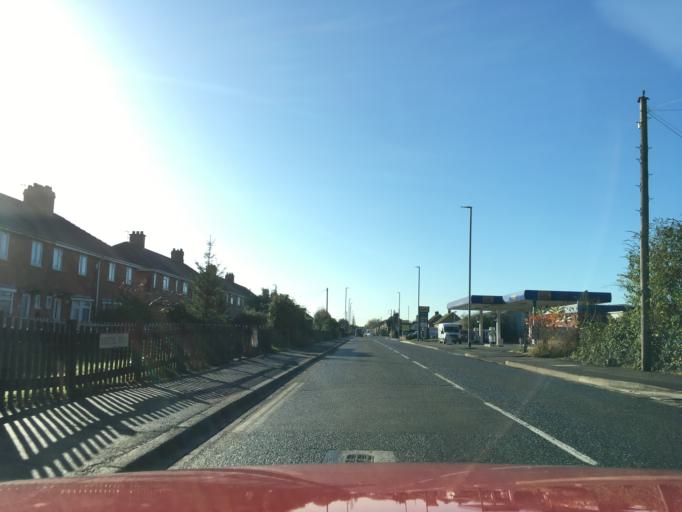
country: GB
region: England
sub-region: Somerset
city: Bridgwater
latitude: 51.1369
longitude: -2.9934
